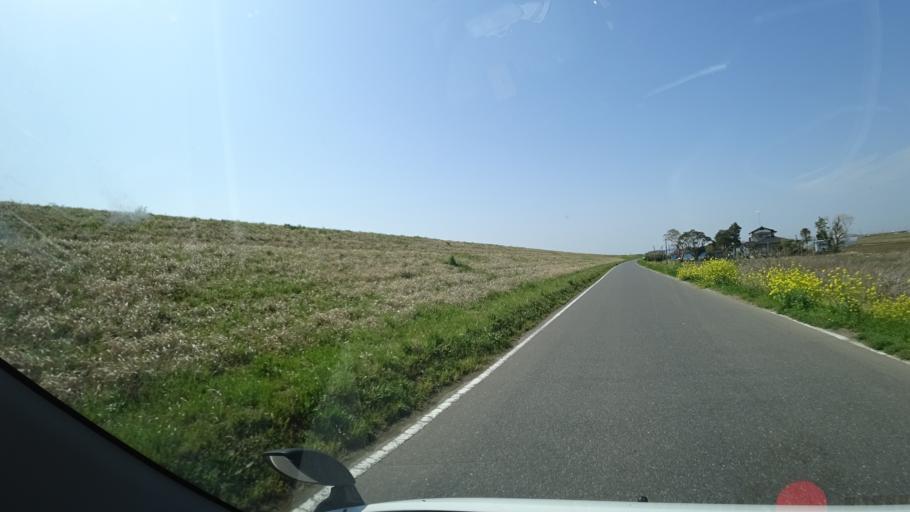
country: JP
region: Ibaraki
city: Edosaki
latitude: 35.8696
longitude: 140.3234
